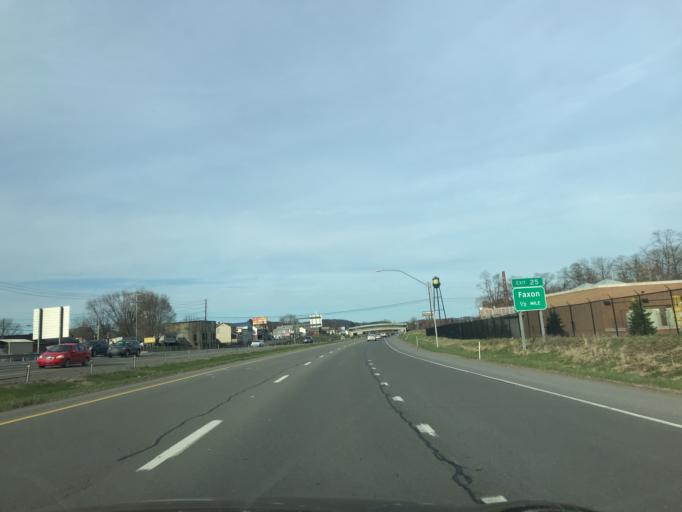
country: US
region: Pennsylvania
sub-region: Lycoming County
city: Williamsport
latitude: 41.2449
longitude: -76.9905
